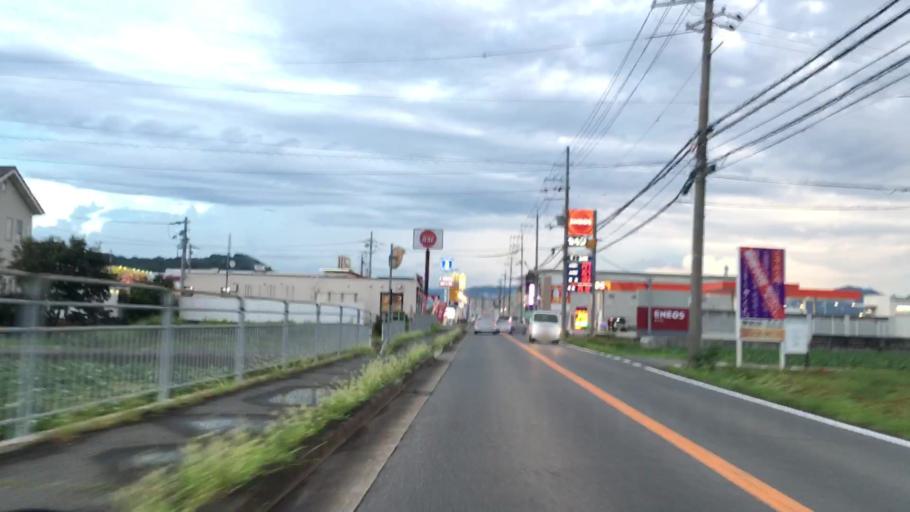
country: JP
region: Hyogo
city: Himeji
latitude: 34.9201
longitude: 134.7426
